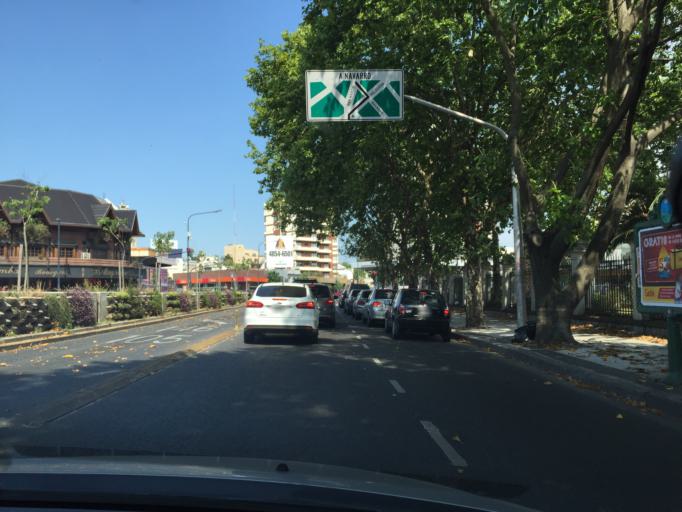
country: AR
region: Buenos Aires F.D.
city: Villa Santa Rita
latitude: -34.5968
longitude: -58.4961
